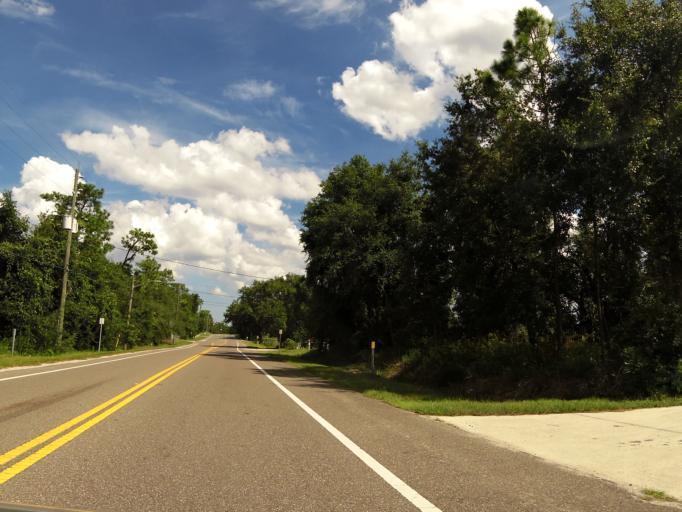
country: US
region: Florida
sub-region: Duval County
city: Jacksonville
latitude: 30.4237
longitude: -81.5743
